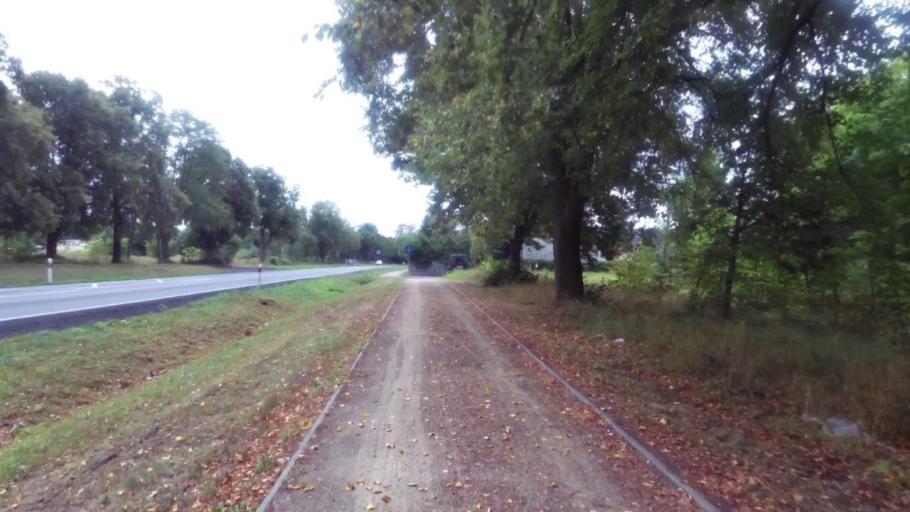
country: PL
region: West Pomeranian Voivodeship
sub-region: Powiat mysliborski
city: Debno
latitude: 52.7256
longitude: 14.6937
